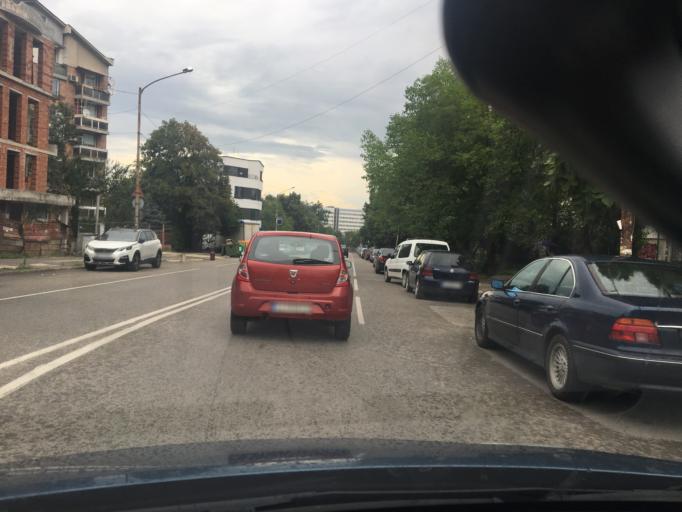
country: BG
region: Sofia-Capital
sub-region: Stolichna Obshtina
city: Sofia
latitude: 42.6647
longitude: 23.2659
